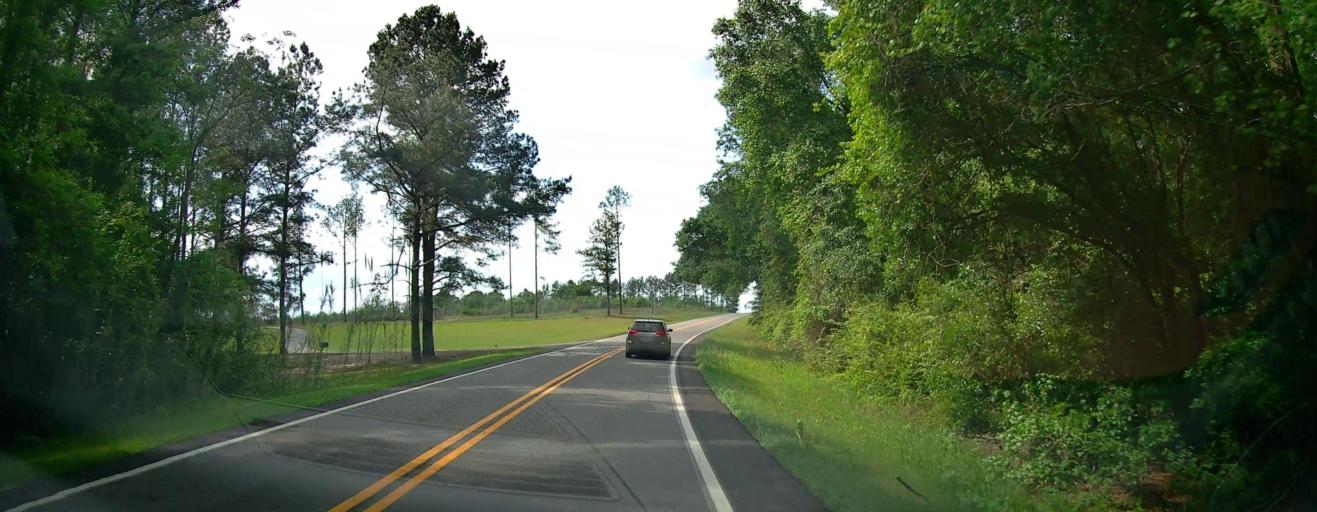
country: US
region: Georgia
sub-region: Laurens County
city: East Dublin
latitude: 32.6330
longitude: -82.8935
